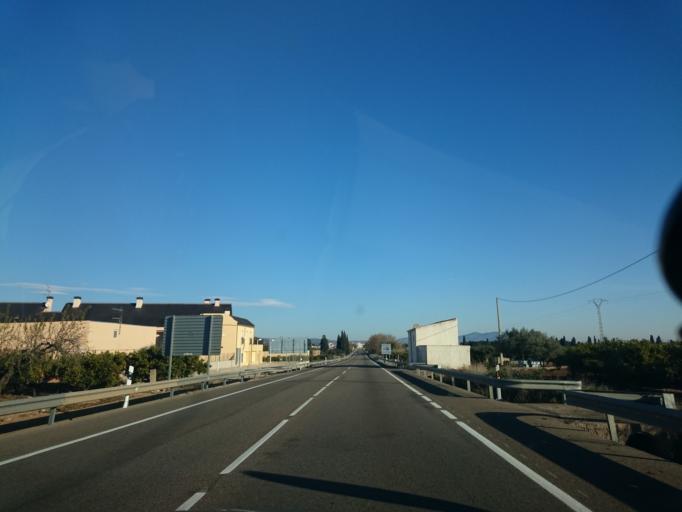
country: ES
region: Valencia
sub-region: Provincia de Castello
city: Orpesa/Oropesa del Mar
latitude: 40.1411
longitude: 0.1525
